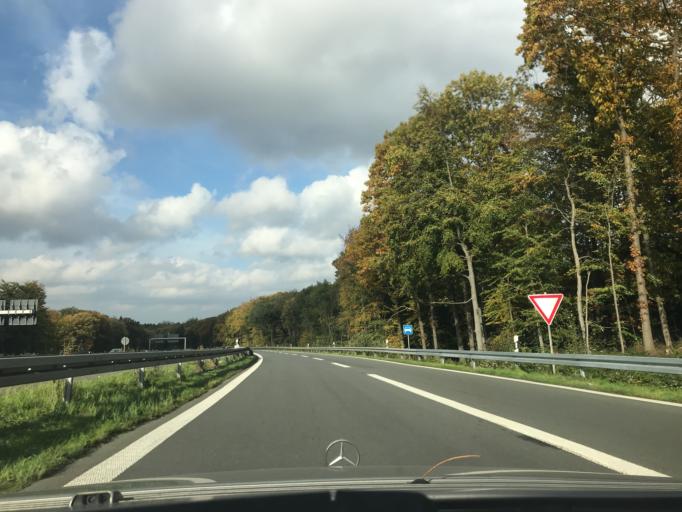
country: DE
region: North Rhine-Westphalia
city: Herdecke
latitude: 51.4458
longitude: 7.4865
